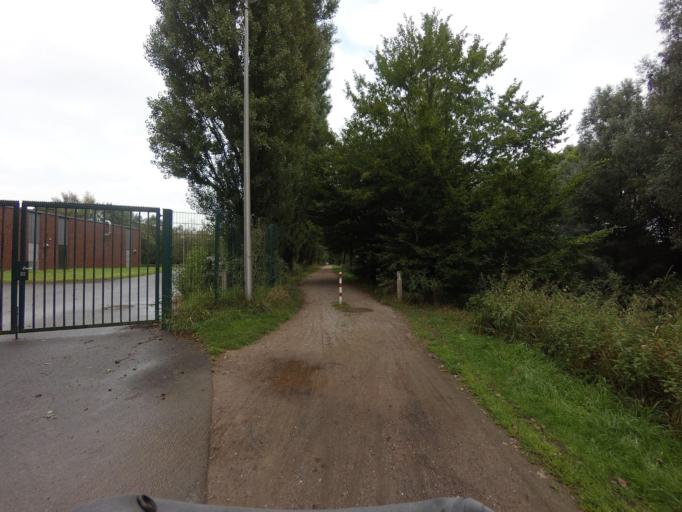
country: DE
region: North Rhine-Westphalia
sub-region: Regierungsbezirk Munster
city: Gronau
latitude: 52.2206
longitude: 7.0242
